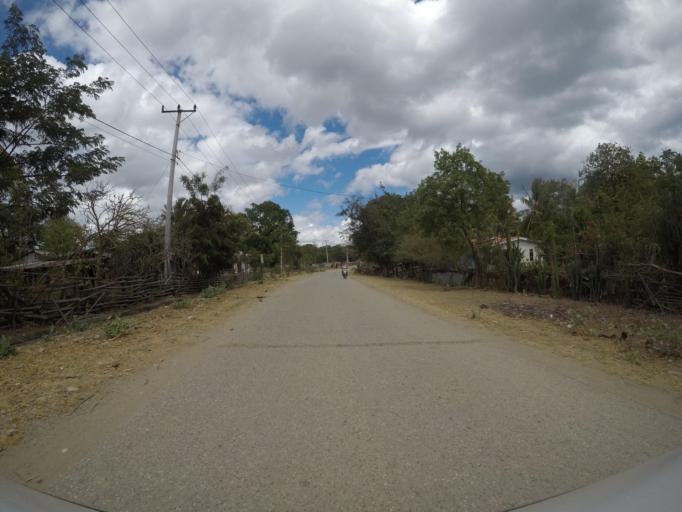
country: TL
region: Lautem
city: Lospalos
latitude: -8.3629
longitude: 126.9043
